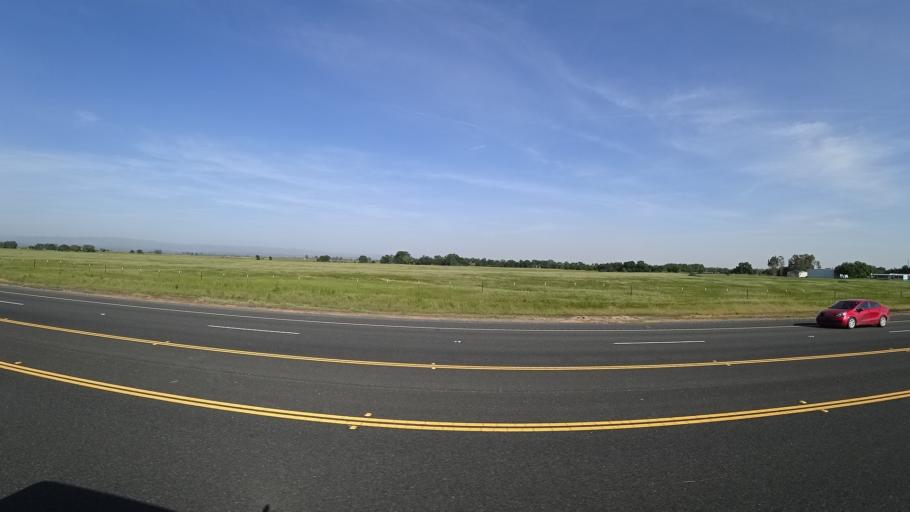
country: US
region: California
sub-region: Butte County
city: Gridley
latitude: 39.3862
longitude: -121.6110
